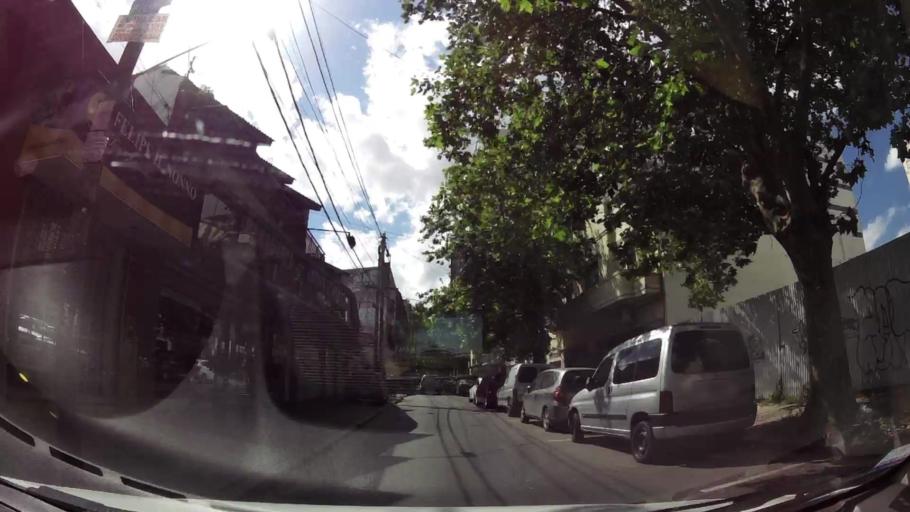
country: AR
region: Buenos Aires
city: San Justo
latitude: -34.6453
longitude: -58.5601
